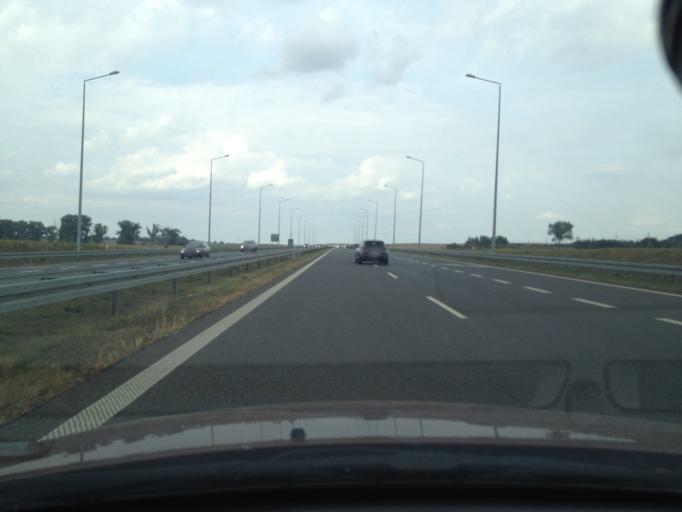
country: PL
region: West Pomeranian Voivodeship
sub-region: Powiat pyrzycki
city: Kozielice
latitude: 53.0543
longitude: 14.8652
